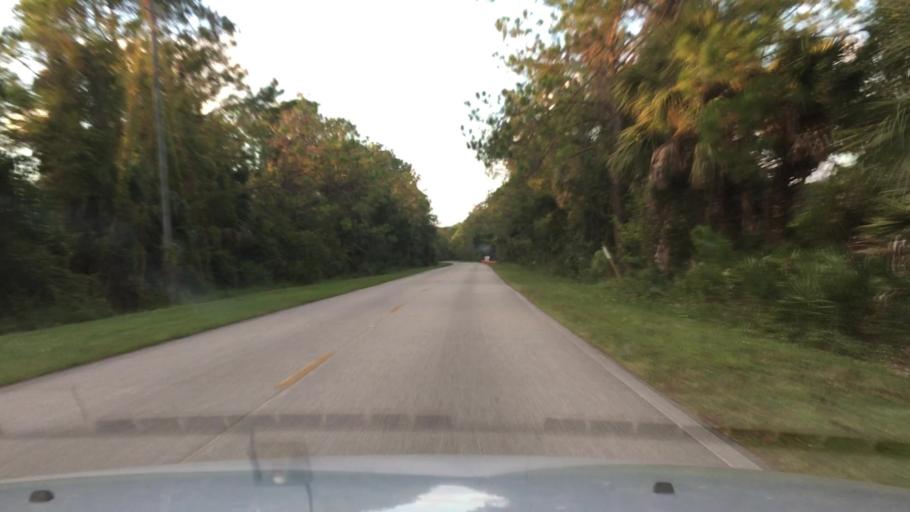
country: US
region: Florida
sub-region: Volusia County
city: Ormond Beach
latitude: 29.2774
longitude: -81.1224
